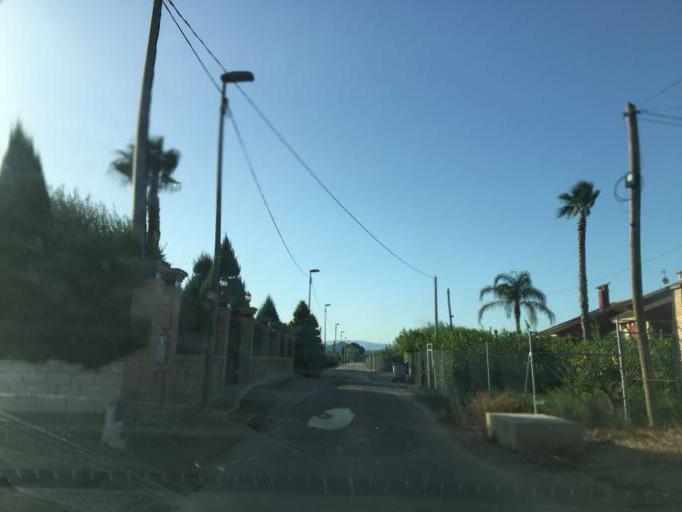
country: ES
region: Murcia
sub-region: Murcia
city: Santomera
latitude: 38.0216
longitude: -1.0561
